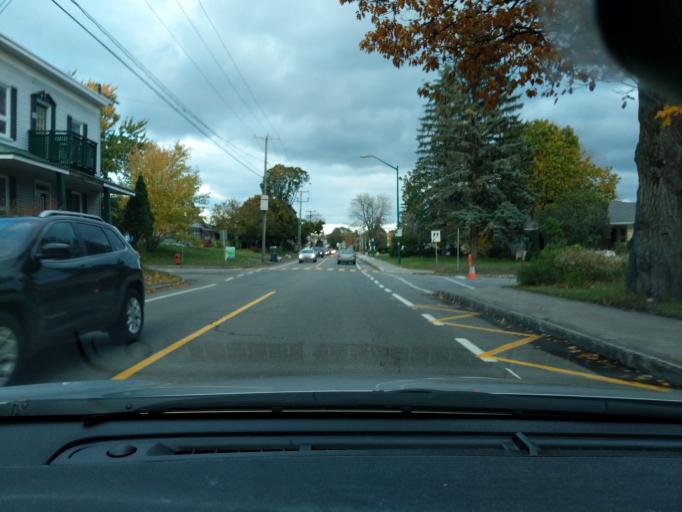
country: CA
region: Quebec
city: L'Ancienne-Lorette
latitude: 46.7605
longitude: -71.2854
